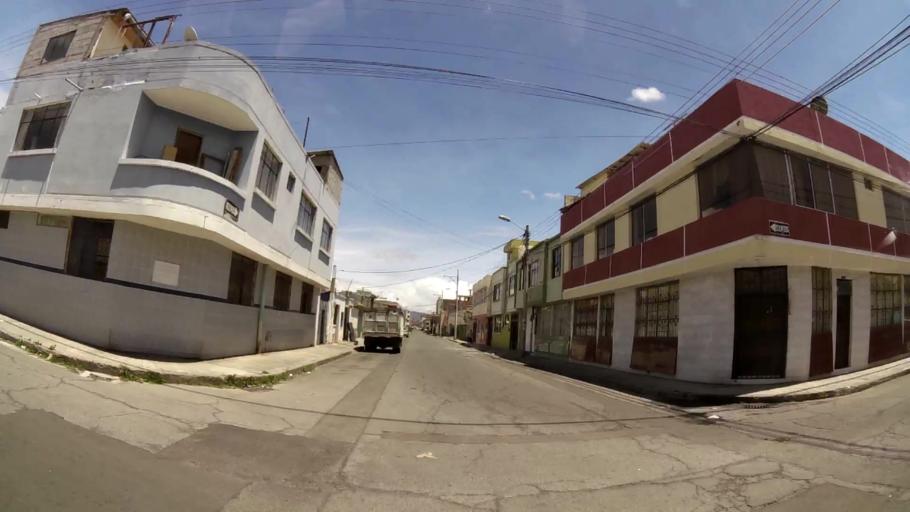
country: EC
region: Chimborazo
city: Riobamba
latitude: -1.6787
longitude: -78.6556
